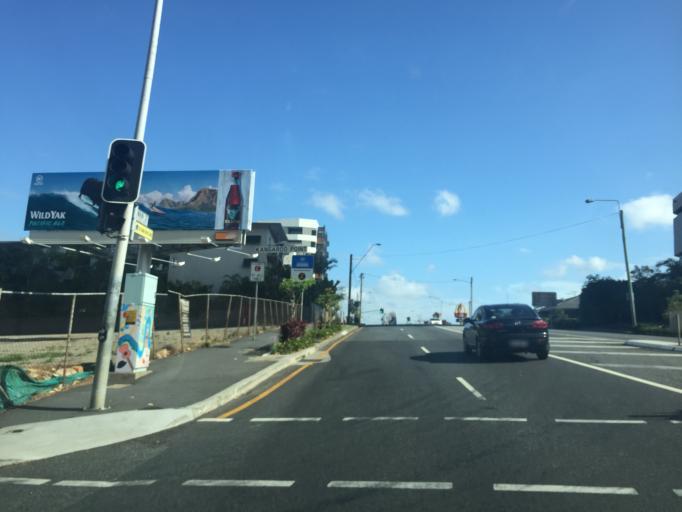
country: AU
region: Queensland
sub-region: Brisbane
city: Woolloongabba
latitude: -27.4845
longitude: 153.0358
